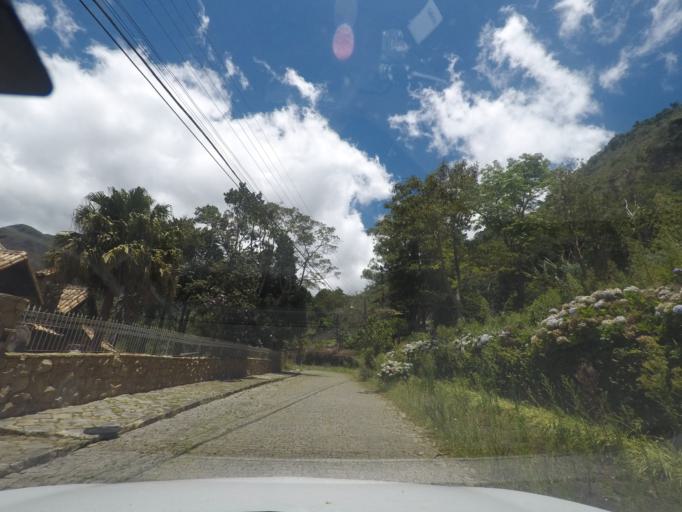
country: BR
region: Rio de Janeiro
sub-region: Teresopolis
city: Teresopolis
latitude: -22.4312
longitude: -42.9958
